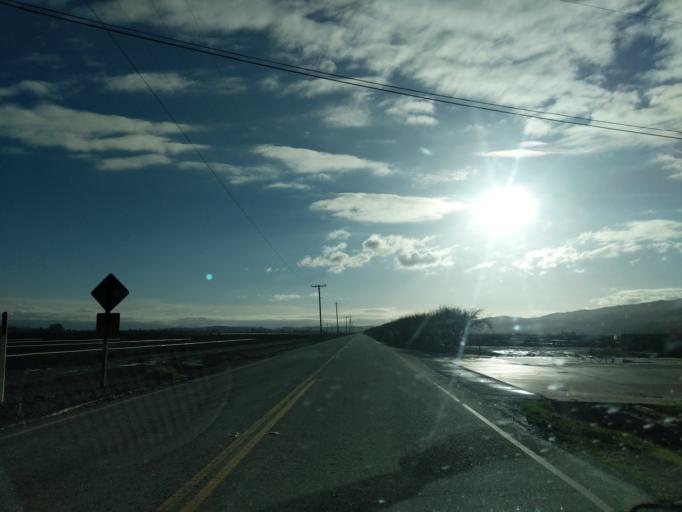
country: US
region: California
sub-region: San Benito County
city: San Juan Bautista
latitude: 36.8603
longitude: -121.5348
